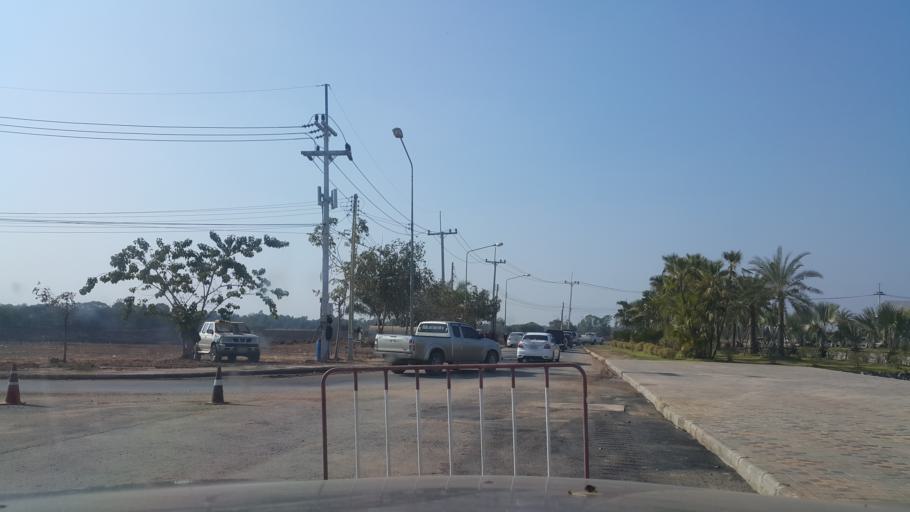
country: TH
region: Khon Kaen
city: Khon Kaen
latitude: 16.5106
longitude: 102.8689
